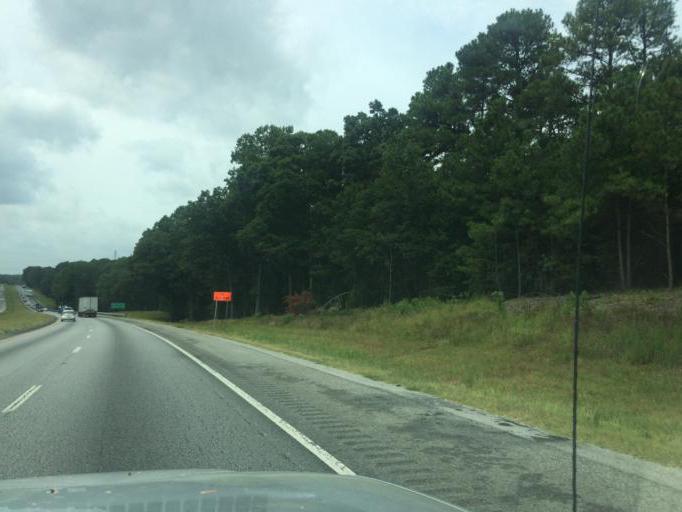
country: US
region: South Carolina
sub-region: Anderson County
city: Northlake
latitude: 34.5726
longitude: -82.7238
